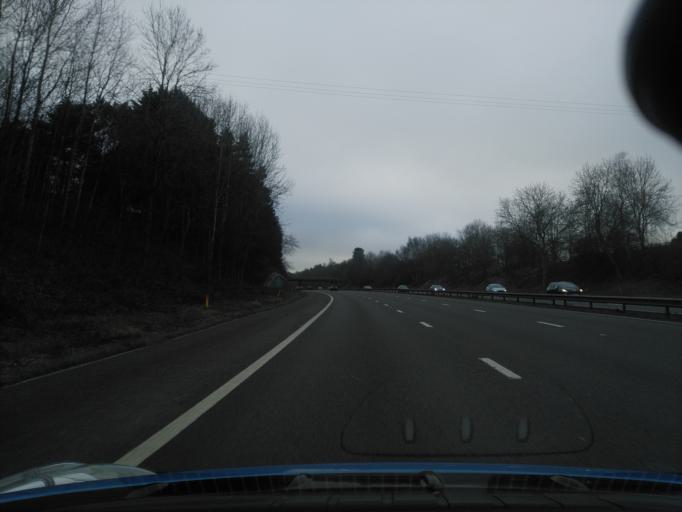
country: GB
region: England
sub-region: Hertfordshire
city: Welwyn Garden City
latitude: 51.8137
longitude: -0.2257
